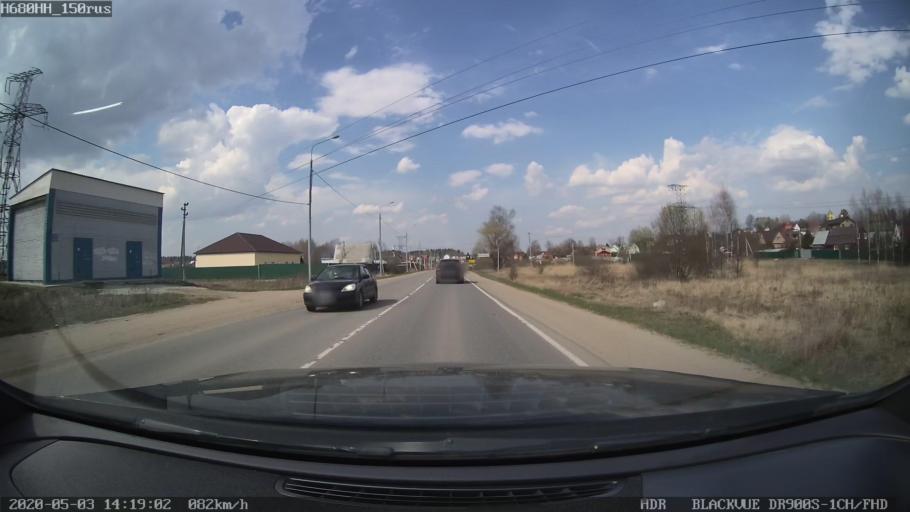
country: RU
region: Moskovskaya
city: Solnechnogorsk
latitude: 56.2277
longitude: 36.9686
